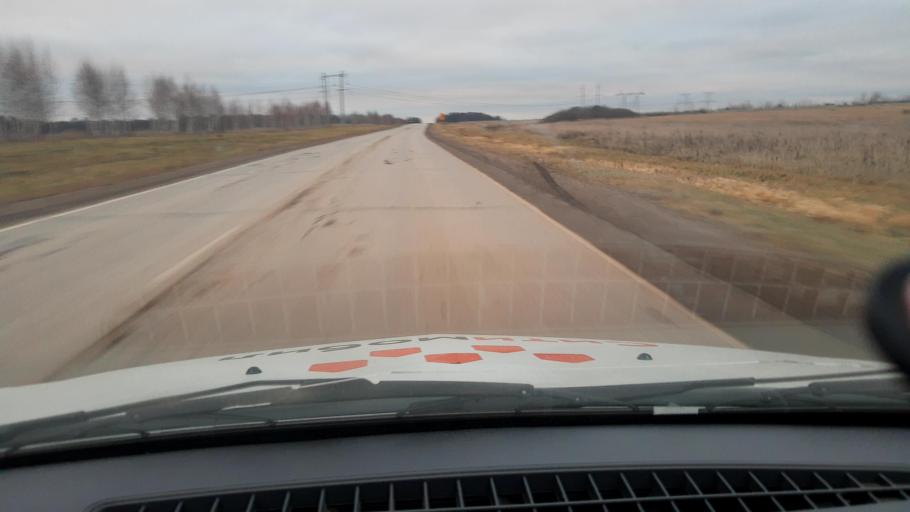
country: RU
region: Bashkortostan
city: Iglino
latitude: 54.7848
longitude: 56.4180
